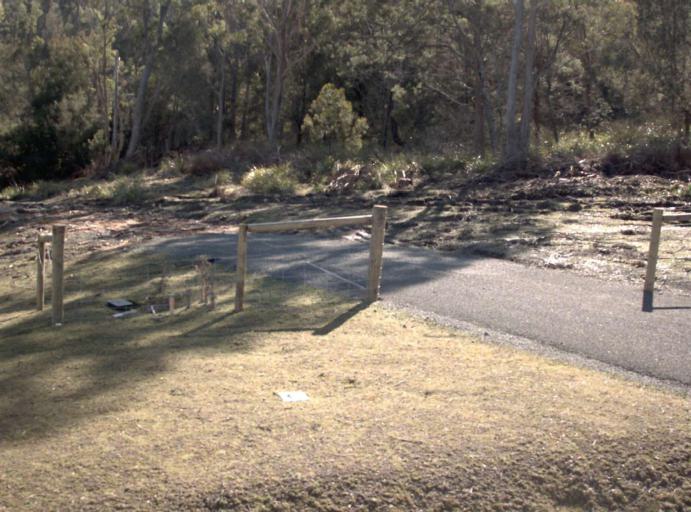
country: AU
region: Tasmania
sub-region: Launceston
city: Mayfield
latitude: -41.2802
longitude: 147.0276
